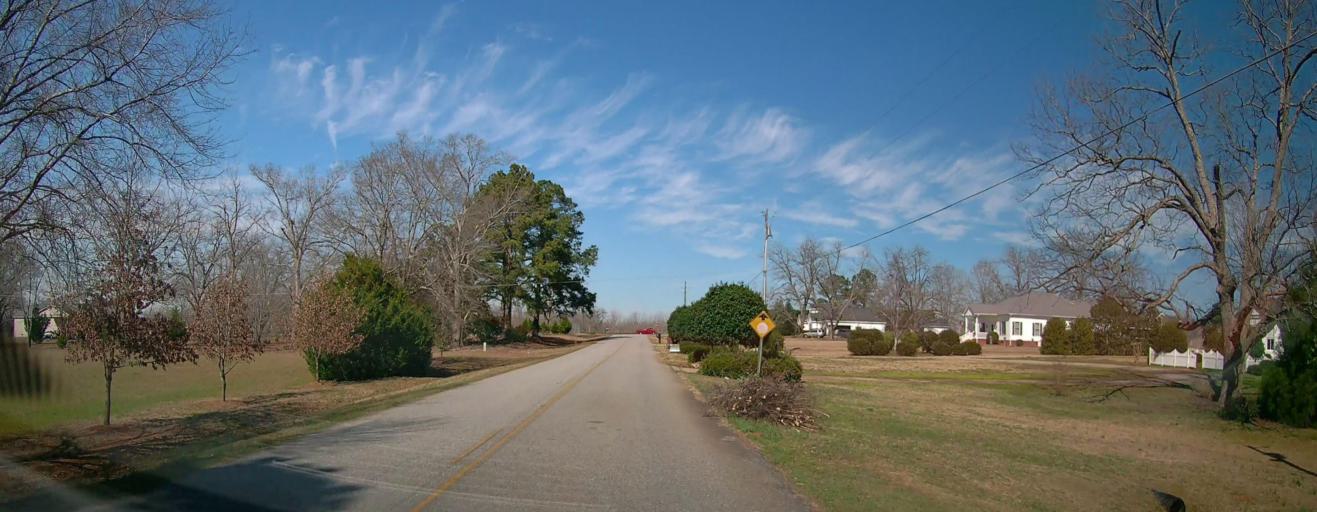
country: US
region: Georgia
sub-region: Houston County
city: Perry
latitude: 32.4527
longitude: -83.6970
